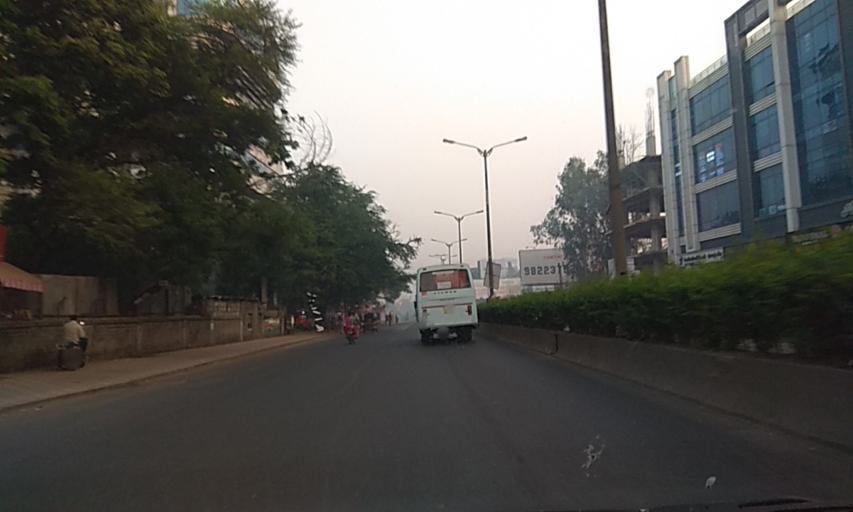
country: IN
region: Maharashtra
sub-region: Pune Division
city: Lohogaon
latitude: 18.5226
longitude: 73.9321
